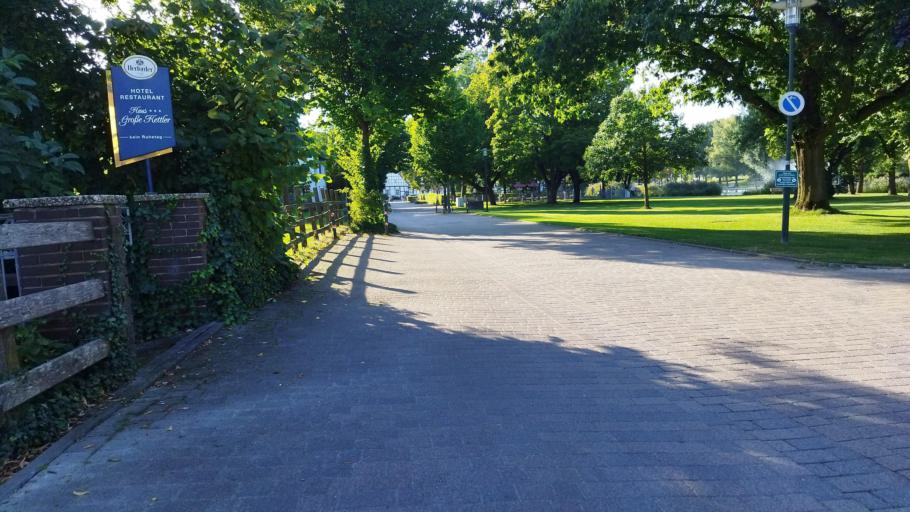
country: DE
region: Lower Saxony
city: Bad Laer
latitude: 52.1038
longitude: 8.0911
